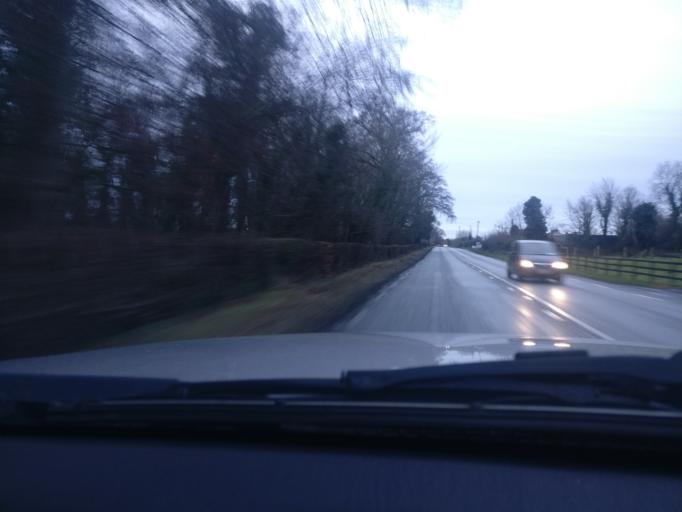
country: IE
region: Leinster
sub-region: An Mhi
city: Navan
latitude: 53.6721
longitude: -6.7387
